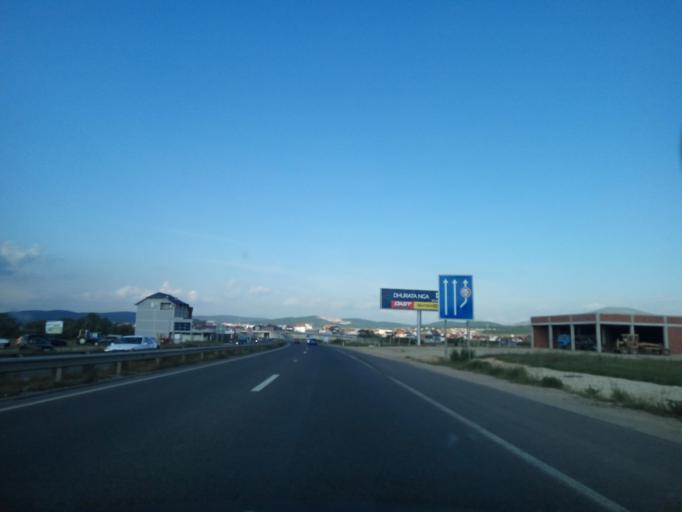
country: XK
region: Pristina
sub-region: Komuna e Drenasit
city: Glogovac
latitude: 42.5768
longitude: 20.8900
